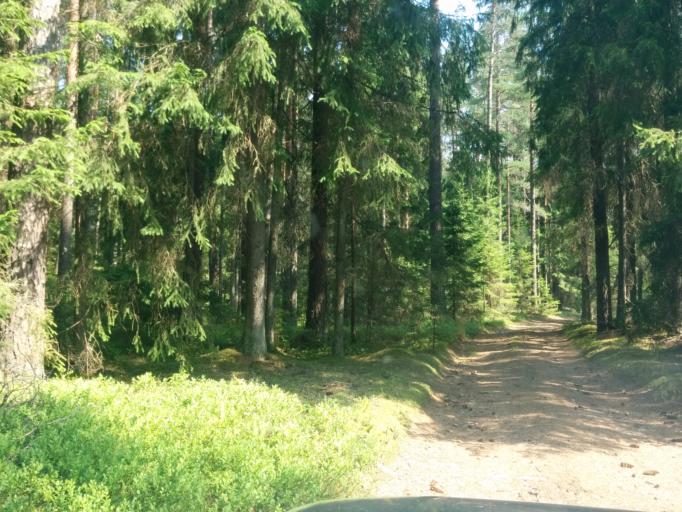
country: LV
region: Ikskile
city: Ikskile
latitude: 56.7419
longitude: 24.5058
